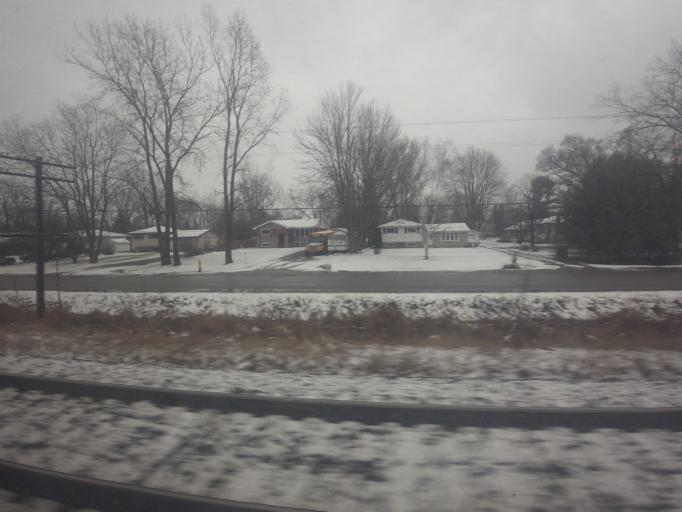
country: CA
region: Ontario
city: Belleville
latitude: 44.1551
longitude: -77.4624
